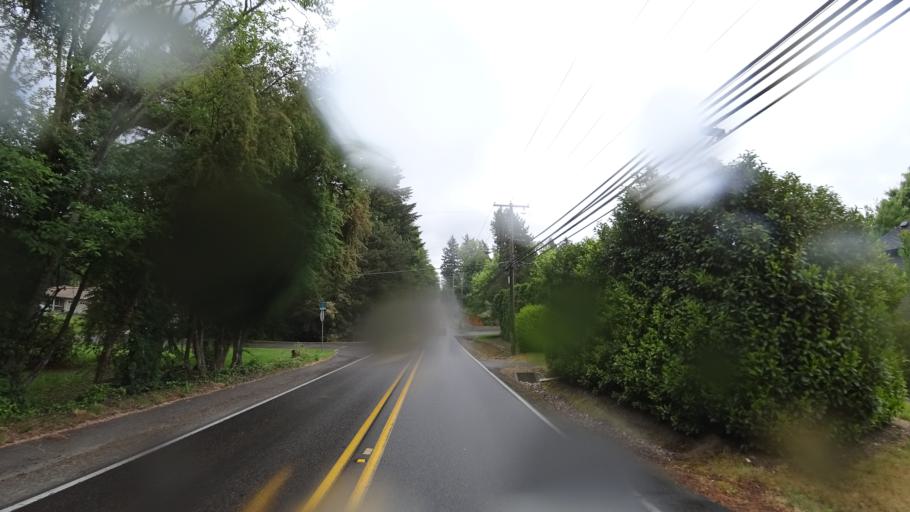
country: US
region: Oregon
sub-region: Washington County
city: Garden Home-Whitford
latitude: 45.4658
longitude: -122.7694
